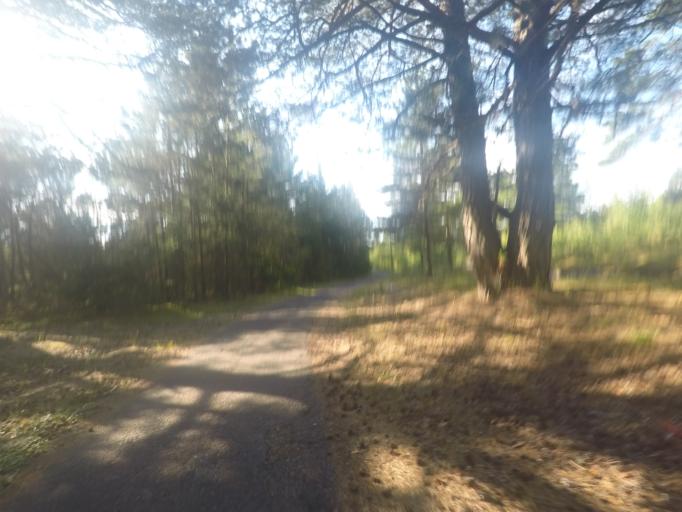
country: LT
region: Klaipedos apskritis
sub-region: Klaipeda
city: Klaipeda
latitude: 55.6063
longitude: 21.1180
